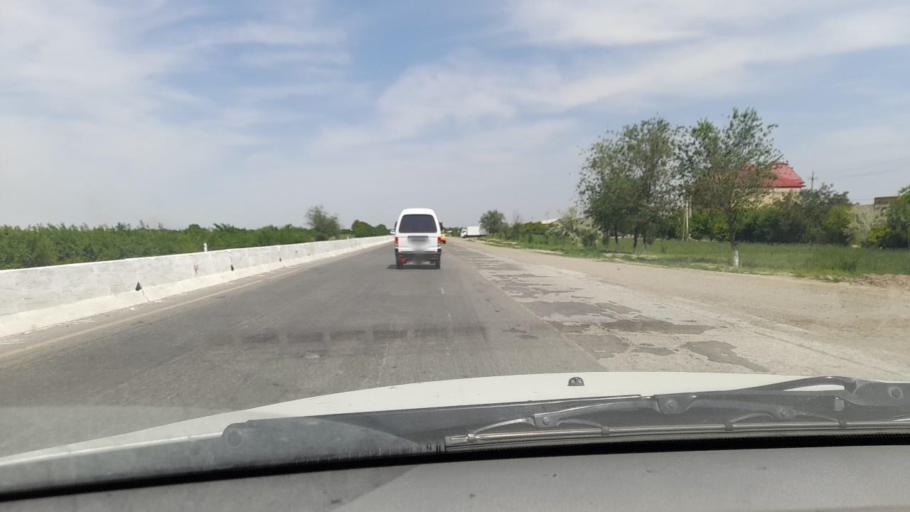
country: UZ
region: Bukhara
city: Wobkent
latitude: 40.0434
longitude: 64.5380
